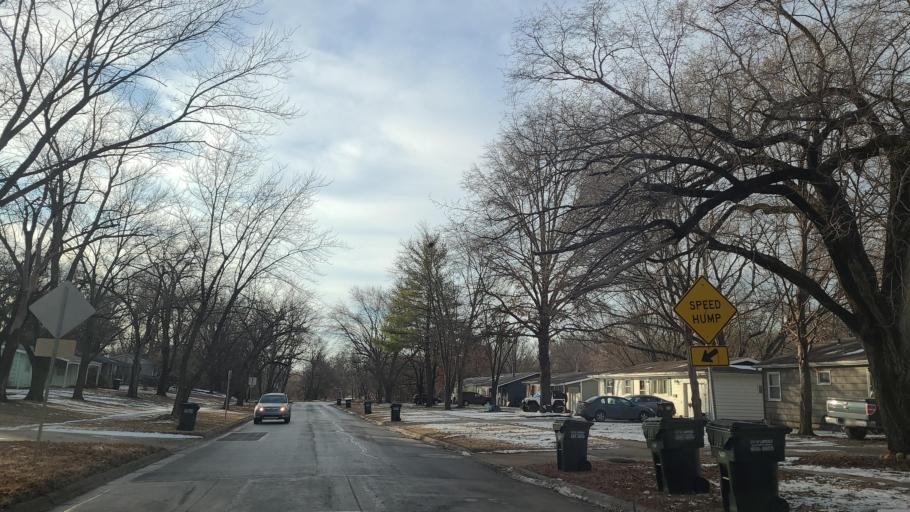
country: US
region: Kansas
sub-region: Douglas County
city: Lawrence
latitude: 38.9656
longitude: -95.2751
